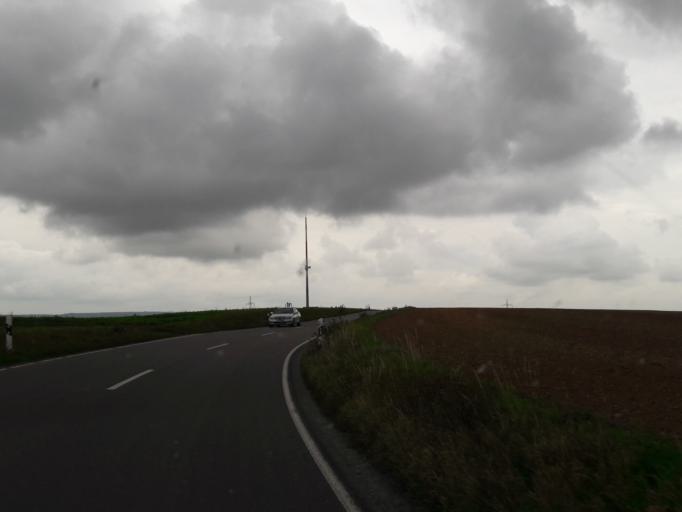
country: DE
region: Baden-Wuerttemberg
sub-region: Regierungsbezirk Stuttgart
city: Neuenstadt am Kocher
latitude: 49.2558
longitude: 9.3458
